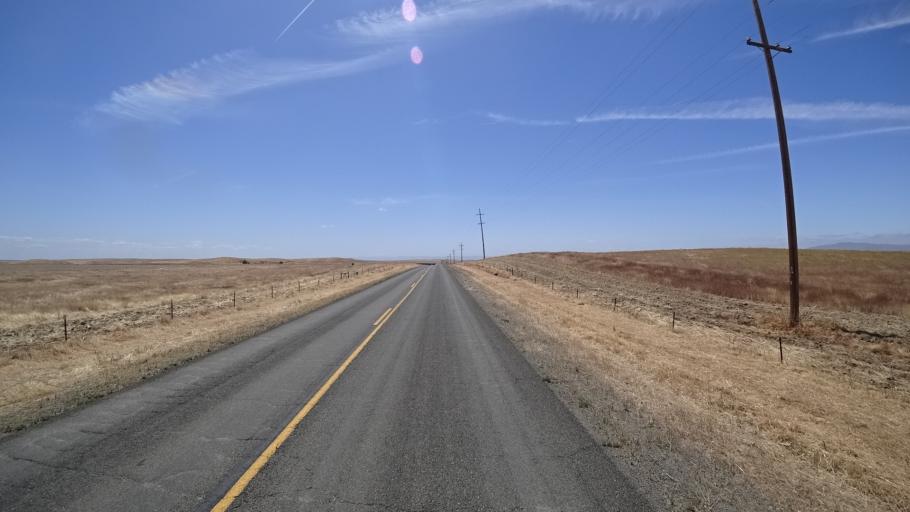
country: US
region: California
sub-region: Kings County
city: Kettleman City
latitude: 35.8546
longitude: -119.9153
